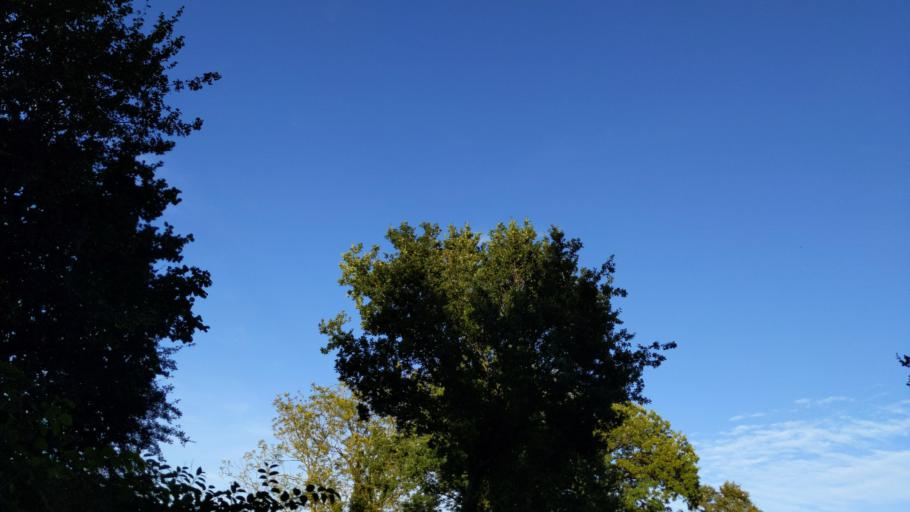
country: DE
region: Schleswig-Holstein
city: Ahrensbok
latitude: 54.0199
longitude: 10.5795
